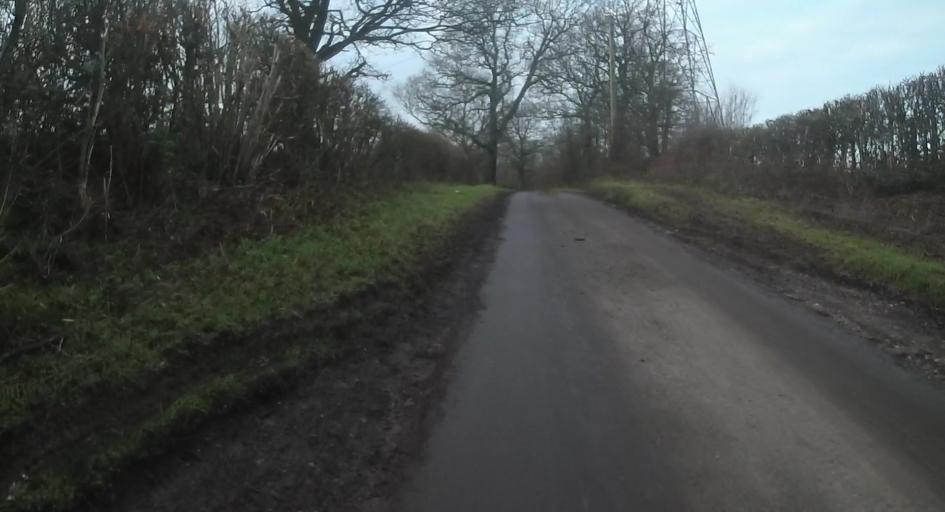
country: GB
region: England
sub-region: Hampshire
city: Kingsclere
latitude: 51.2997
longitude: -1.2315
